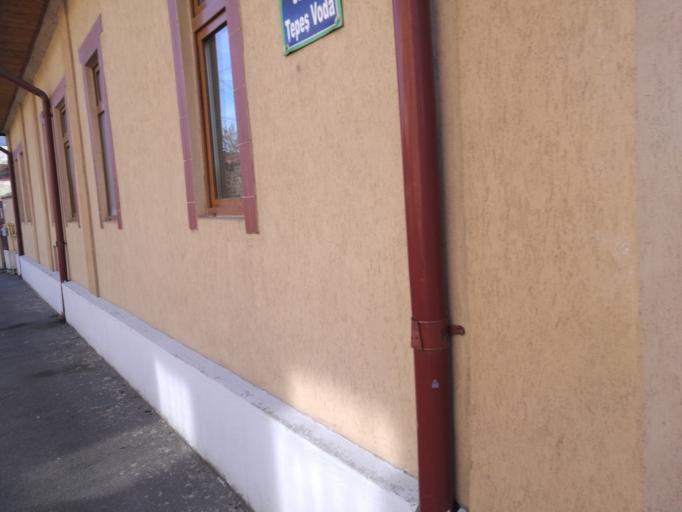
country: RO
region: Bucuresti
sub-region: Municipiul Bucuresti
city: Bucharest
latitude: 44.4356
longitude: 26.1308
